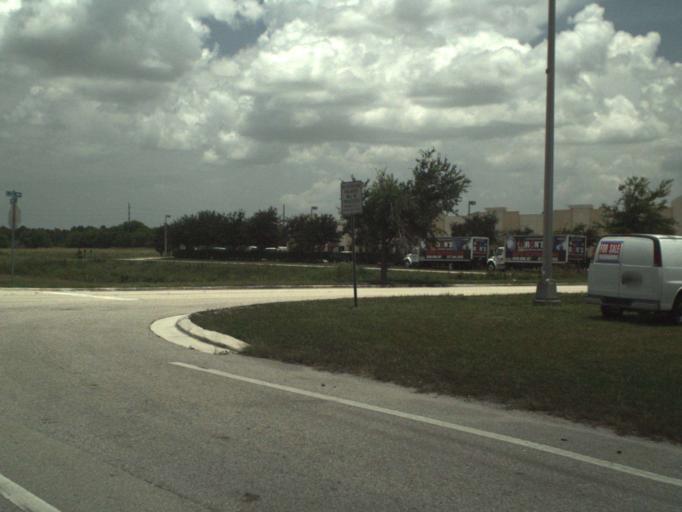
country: US
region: Florida
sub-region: Saint Lucie County
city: Fort Pierce South
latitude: 27.3744
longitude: -80.4010
